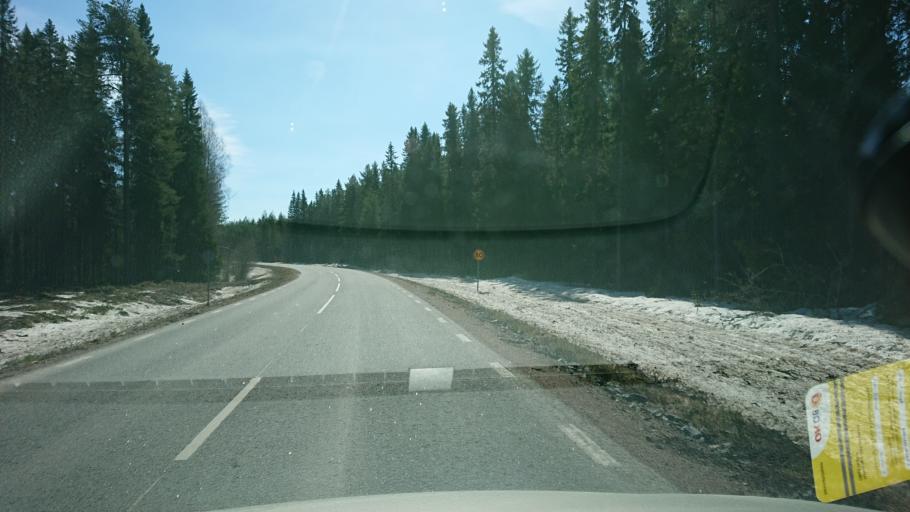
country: SE
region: Vaesternorrland
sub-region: Solleftea Kommun
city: As
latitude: 63.6684
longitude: 16.4311
